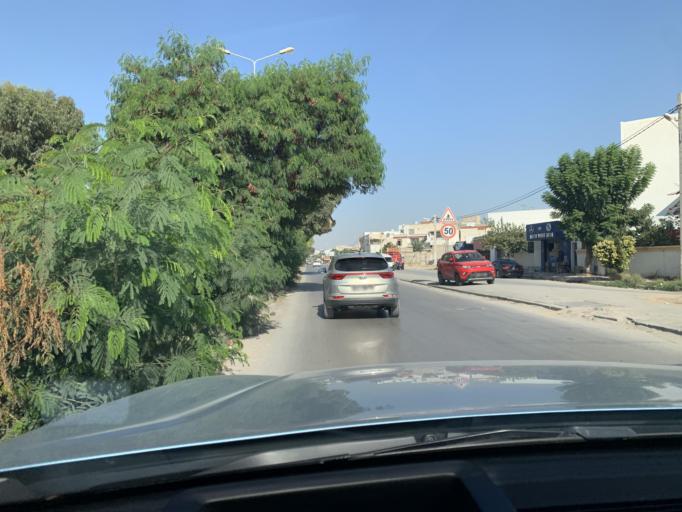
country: TN
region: Manouba
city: Manouba
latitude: 36.8202
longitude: 10.1243
